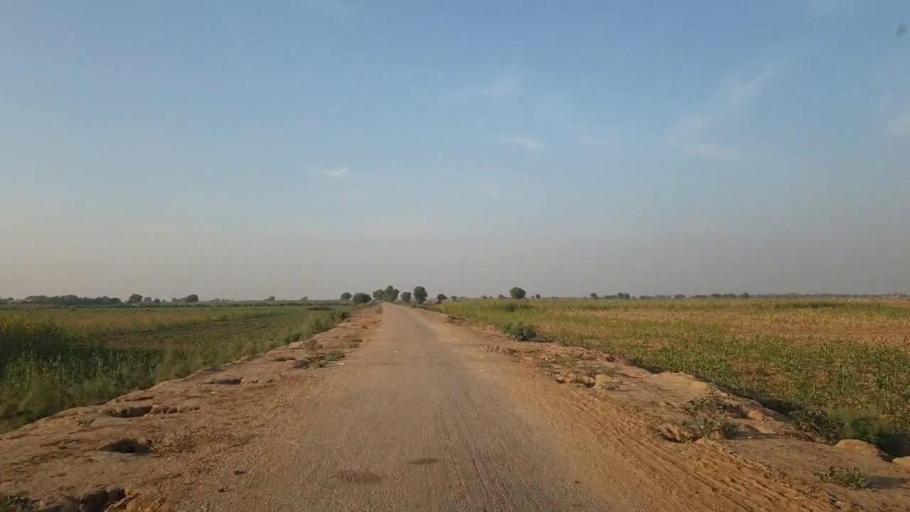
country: PK
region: Sindh
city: Sann
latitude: 25.9240
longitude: 68.1793
